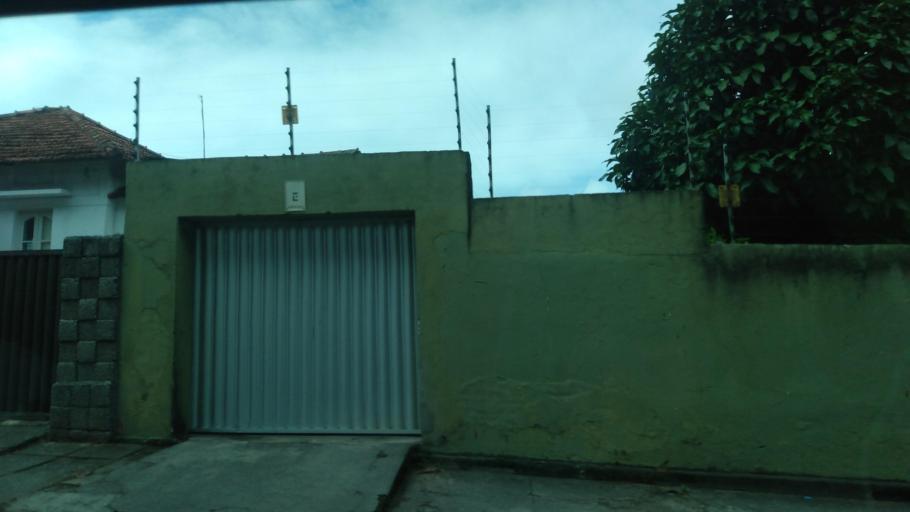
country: BR
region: Pernambuco
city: Garanhuns
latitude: -8.8828
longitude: -36.4793
